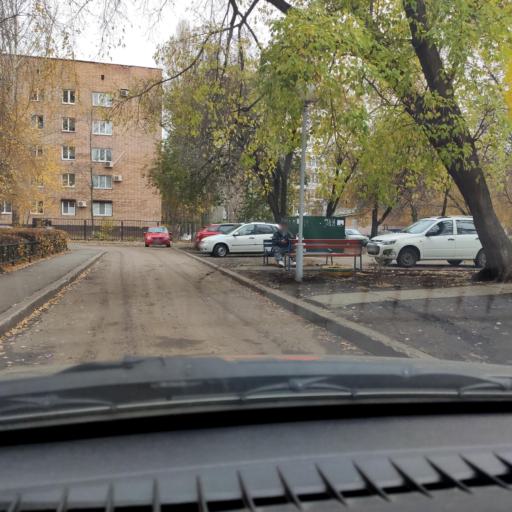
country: RU
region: Samara
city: Tol'yatti
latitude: 53.5239
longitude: 49.3100
